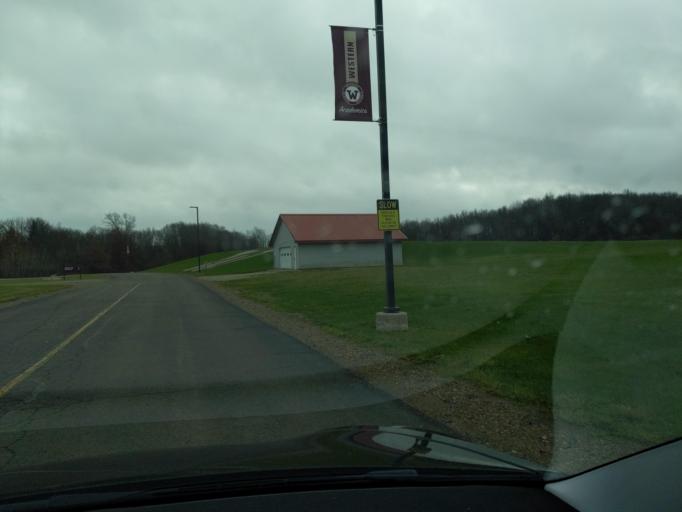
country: US
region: Michigan
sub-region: Jackson County
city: Spring Arbor
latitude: 42.2513
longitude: -84.5397
